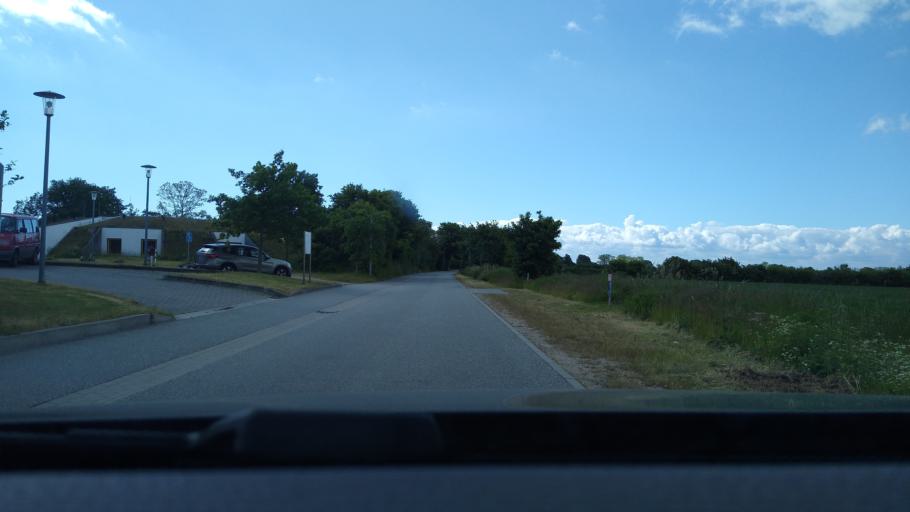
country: DE
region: Schleswig-Holstein
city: Dahme
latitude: 54.2074
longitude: 11.0896
